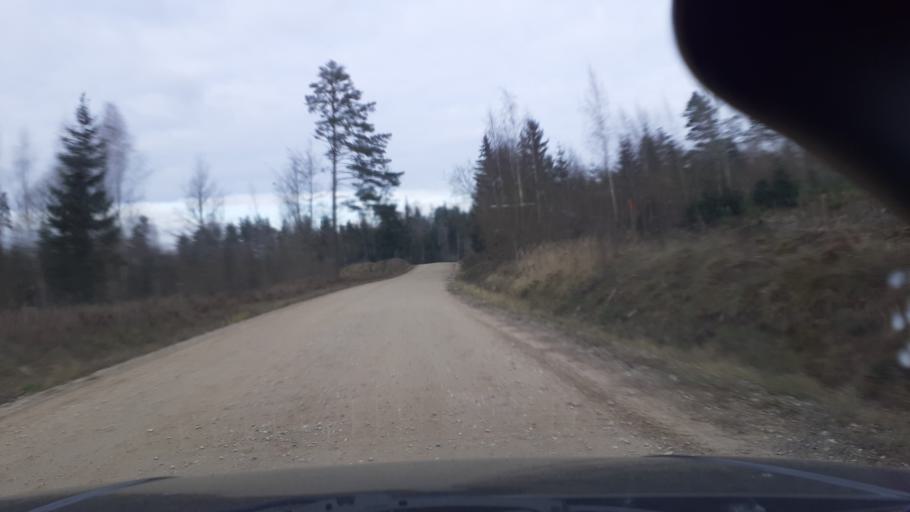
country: LV
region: Alsunga
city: Alsunga
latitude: 56.9827
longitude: 21.6688
